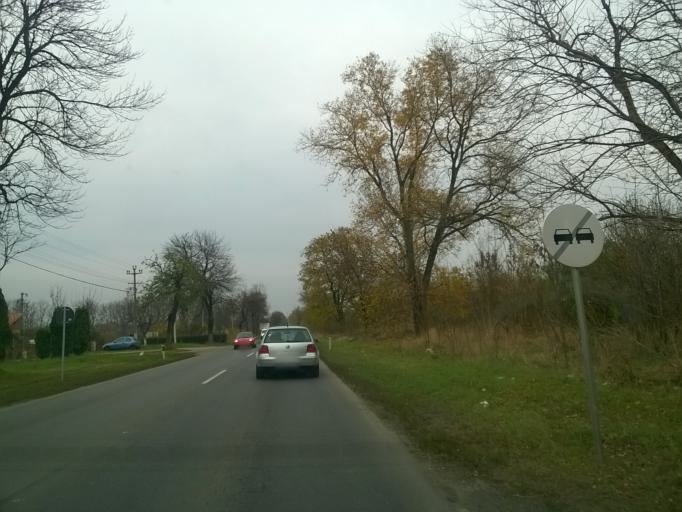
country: RS
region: Autonomna Pokrajina Vojvodina
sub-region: Juznobanatski Okrug
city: Pancevo
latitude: 44.9036
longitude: 20.6315
